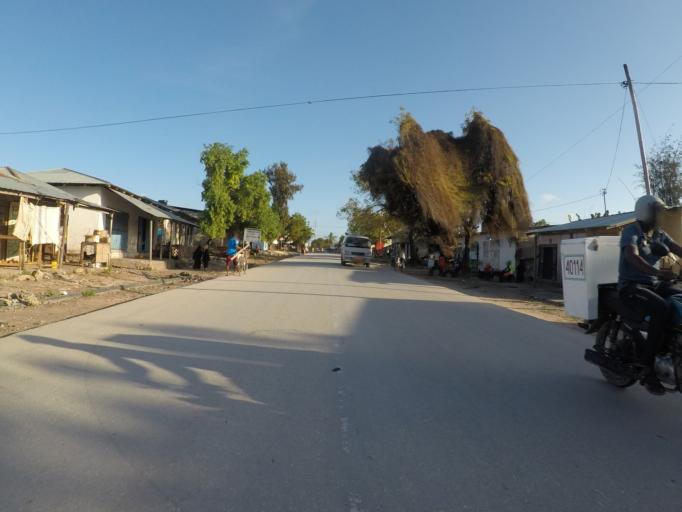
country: TZ
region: Zanzibar North
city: Nungwi
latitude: -5.7299
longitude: 39.2980
